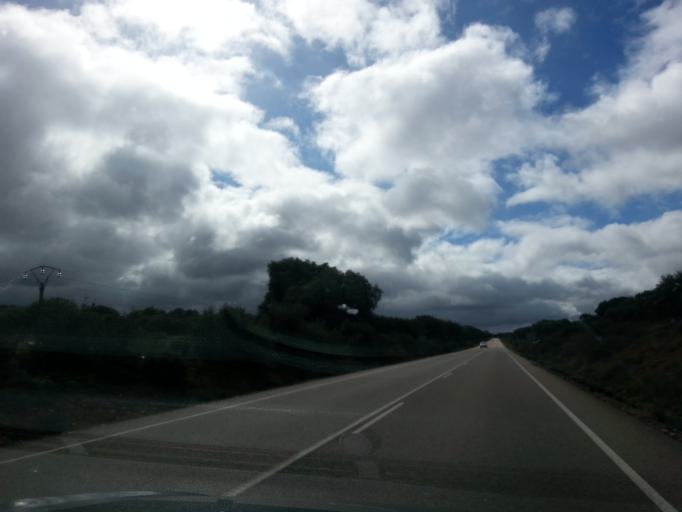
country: ES
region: Castille and Leon
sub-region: Provincia de Salamanca
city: Abusejo
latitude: 40.6935
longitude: -6.1322
